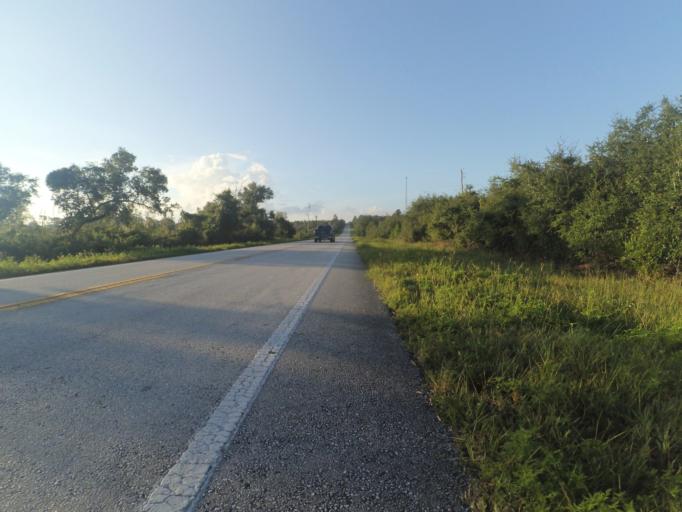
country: US
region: Florida
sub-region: Lake County
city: Astor
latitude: 29.2833
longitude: -81.6510
